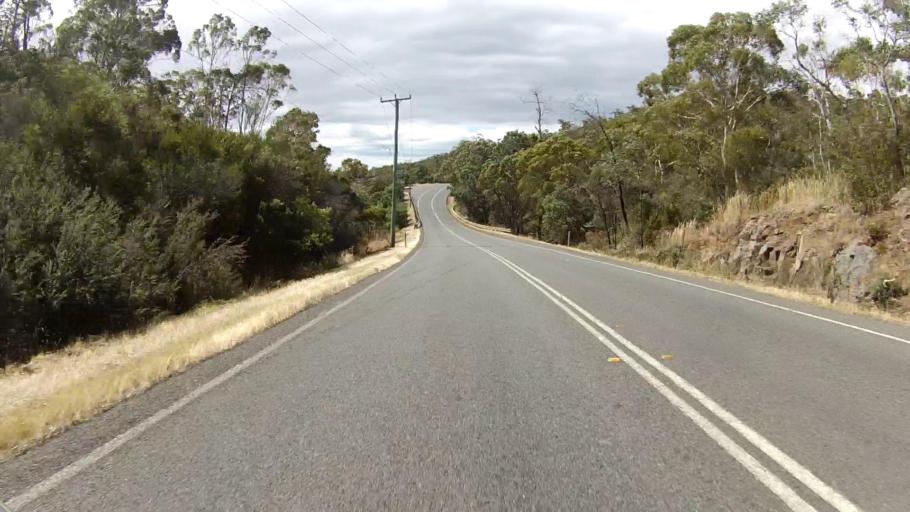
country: AU
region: Tasmania
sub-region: Sorell
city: Sorell
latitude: -42.6072
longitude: 147.6754
